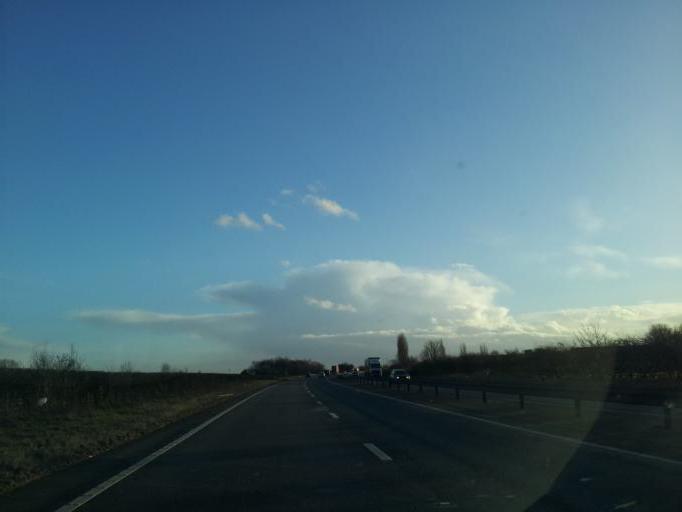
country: GB
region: England
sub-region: Nottinghamshire
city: Newark on Trent
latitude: 53.0633
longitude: -0.7650
